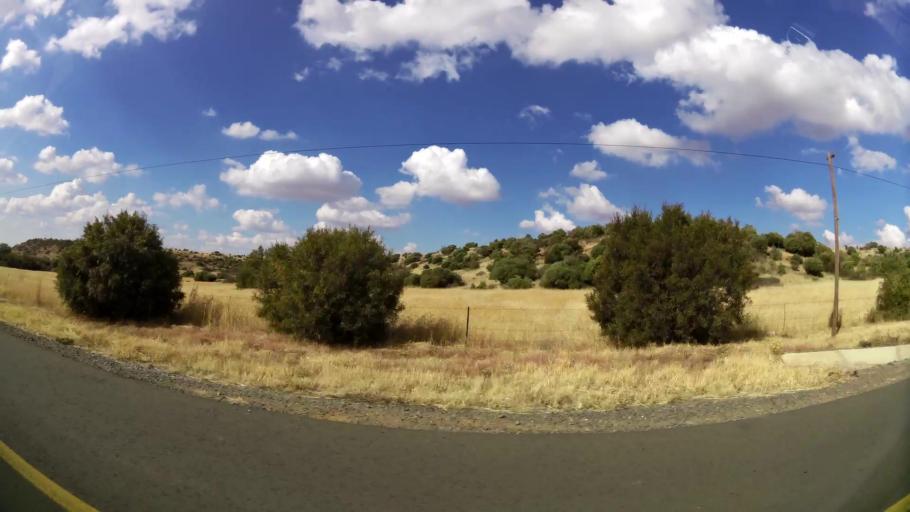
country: ZA
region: Orange Free State
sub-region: Mangaung Metropolitan Municipality
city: Bloemfontein
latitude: -29.1547
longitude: 26.0583
